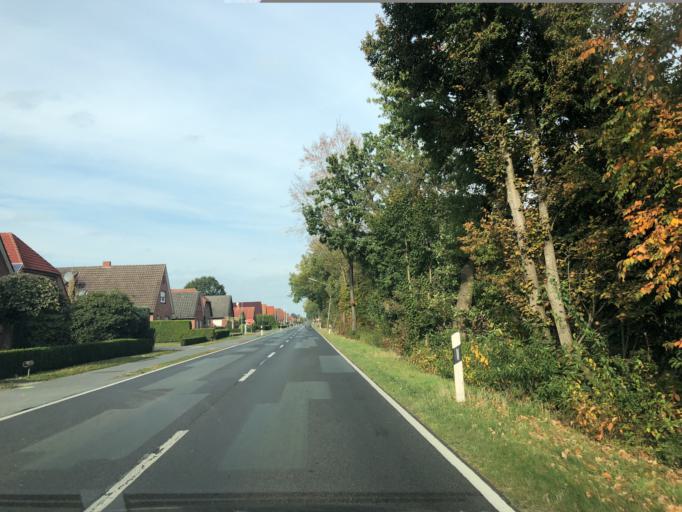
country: DE
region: Lower Saxony
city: Surwold
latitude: 53.0277
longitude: 7.4772
